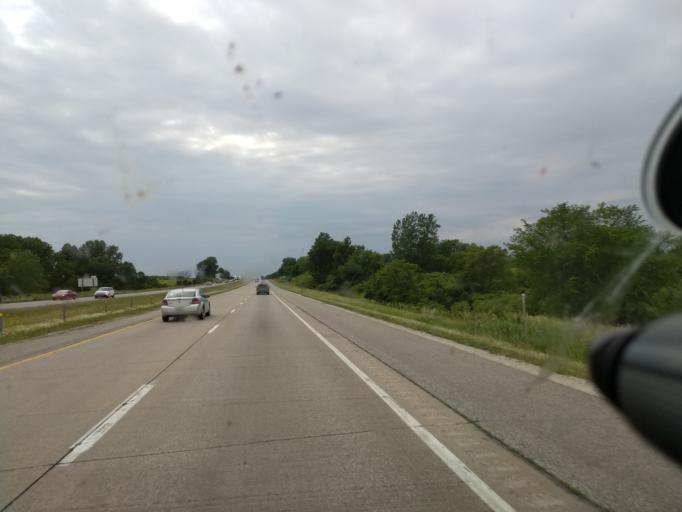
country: US
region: Iowa
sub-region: Dallas County
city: Waukee
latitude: 41.5602
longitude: -93.8948
